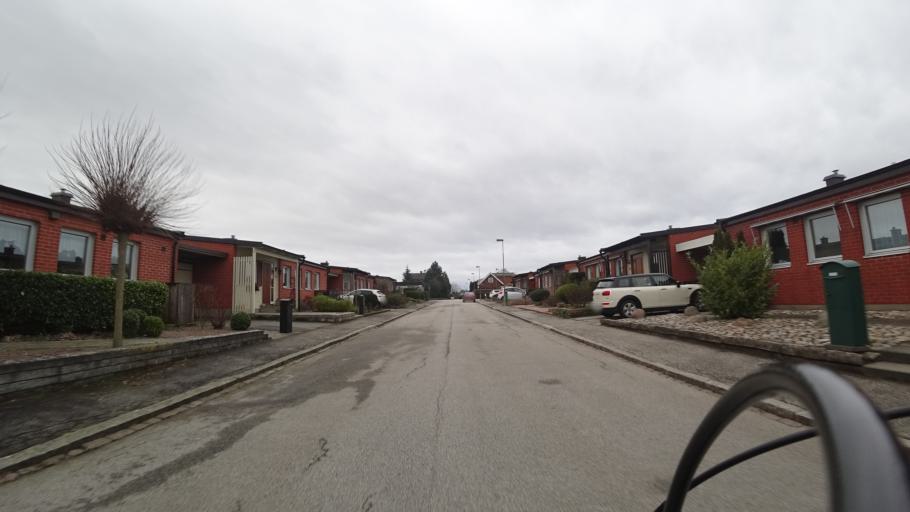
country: SE
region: Skane
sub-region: Malmo
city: Malmoe
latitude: 55.5675
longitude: 12.9999
